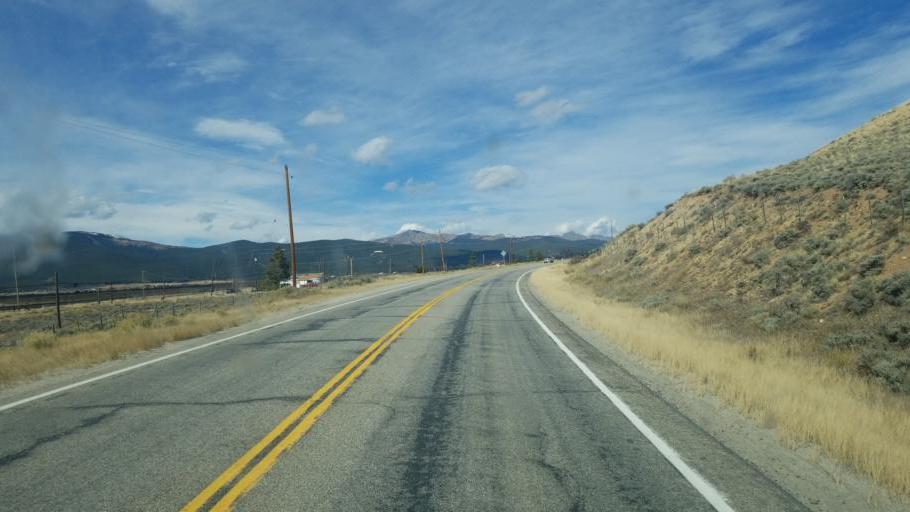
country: US
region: Colorado
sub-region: Lake County
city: Leadville North
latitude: 39.2034
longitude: -106.3437
